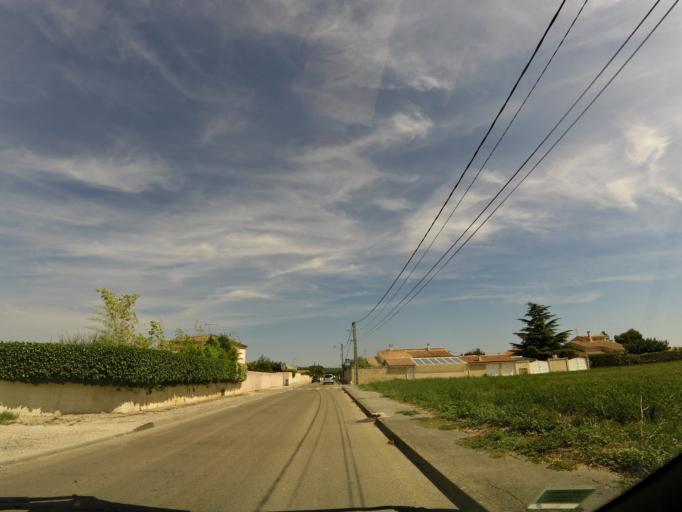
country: FR
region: Languedoc-Roussillon
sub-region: Departement du Gard
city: Calvisson
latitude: 43.7887
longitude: 4.1882
